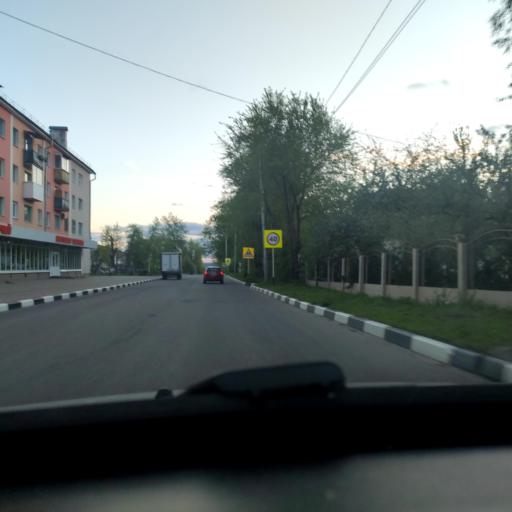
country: RU
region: Voronezj
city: Novovoronezh
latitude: 51.3130
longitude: 39.2175
